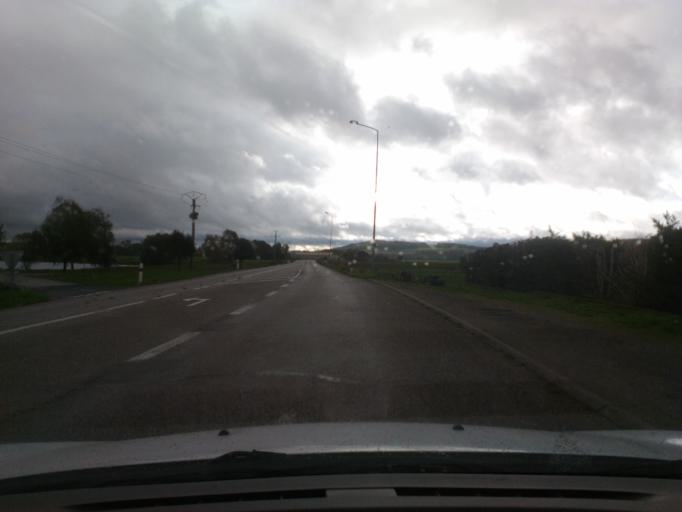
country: FR
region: Lorraine
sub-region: Departement des Vosges
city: Charmes
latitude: 48.3932
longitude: 6.2563
